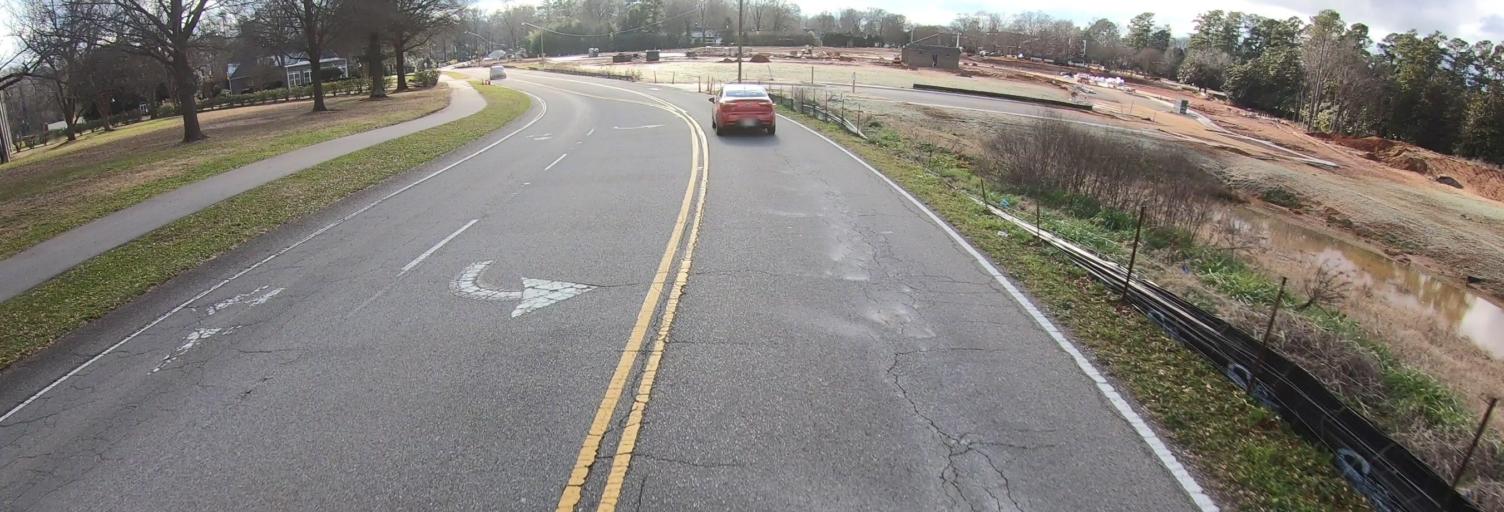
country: US
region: South Carolina
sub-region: York County
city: Rock Hill
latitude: 34.9483
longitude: -81.0194
